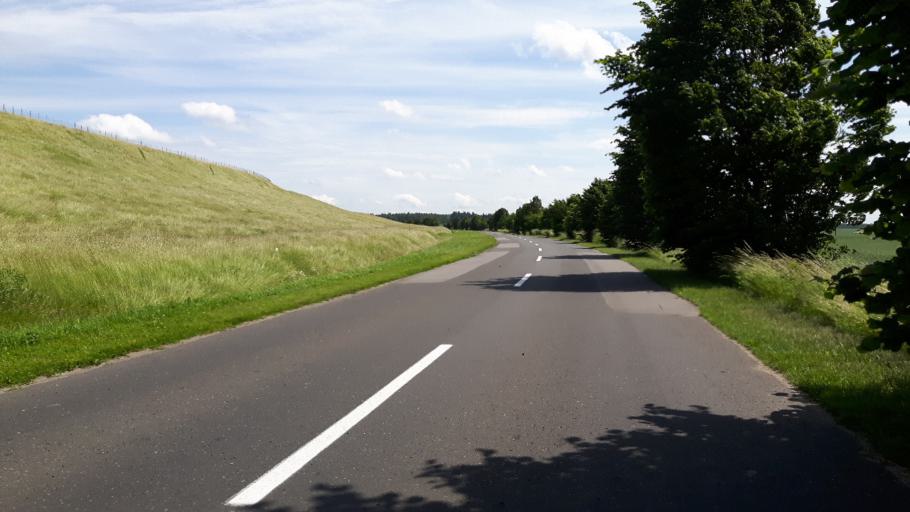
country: PL
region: Pomeranian Voivodeship
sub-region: Powiat wejherowski
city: Gniewino
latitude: 54.7115
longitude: 18.0484
